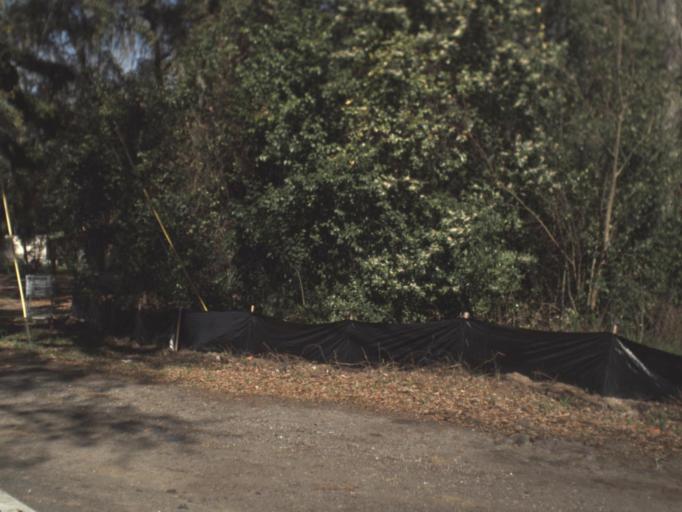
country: US
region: Florida
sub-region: Leon County
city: Tallahassee
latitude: 30.4126
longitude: -84.3003
